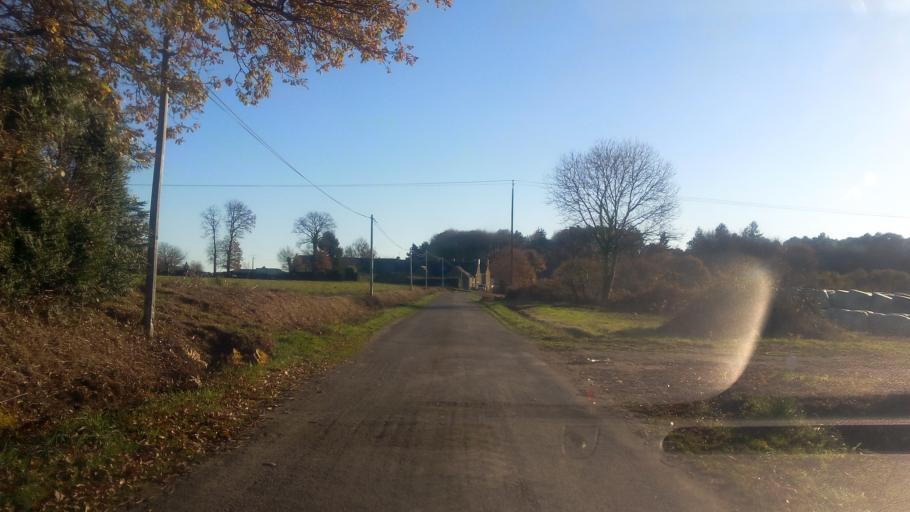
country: FR
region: Brittany
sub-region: Departement du Morbihan
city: Peillac
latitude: 47.7231
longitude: -2.2287
